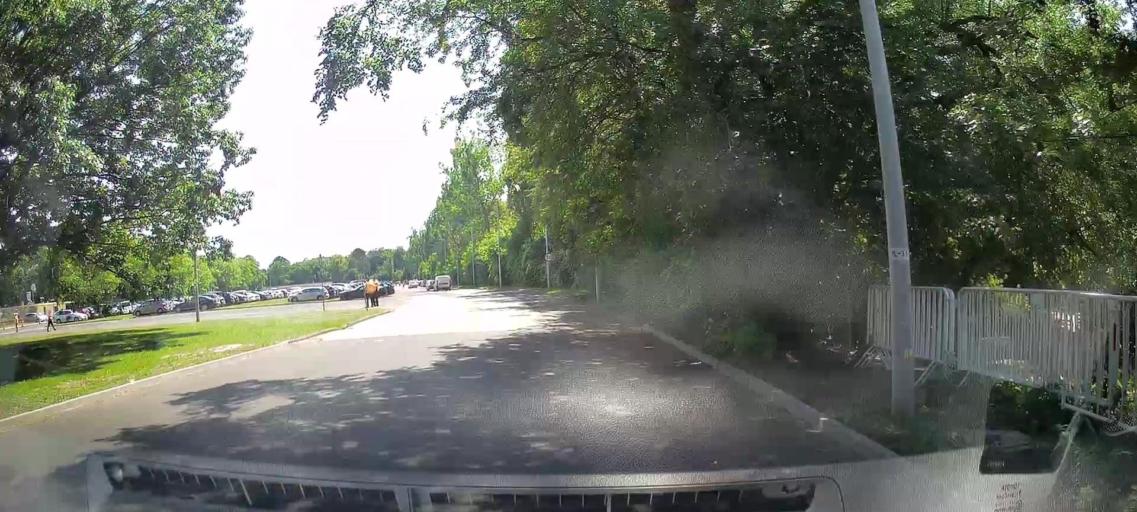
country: PL
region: Masovian Voivodeship
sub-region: Warszawa
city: Mokotow
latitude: 52.1619
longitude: 21.0068
